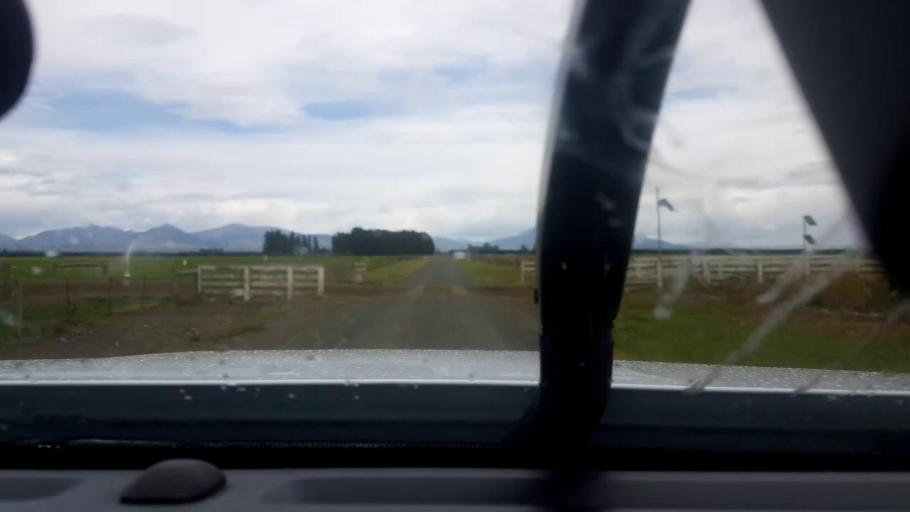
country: NZ
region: Canterbury
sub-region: Timaru District
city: Pleasant Point
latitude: -44.1138
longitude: 171.3544
